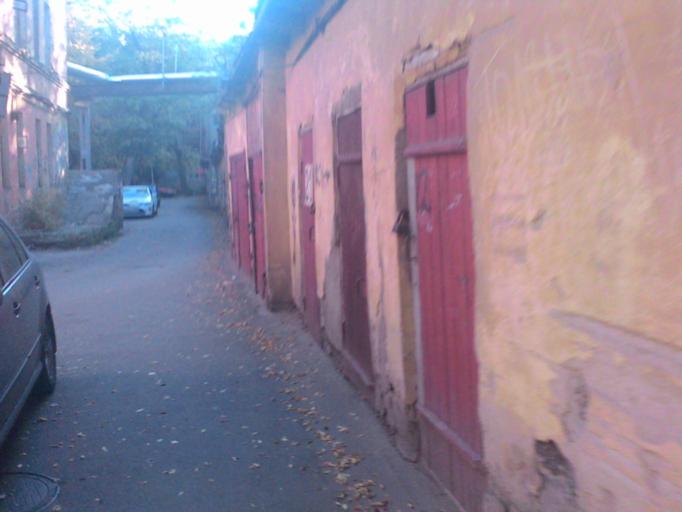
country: RU
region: Voronezj
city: Voronezh
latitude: 51.6680
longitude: 39.1906
